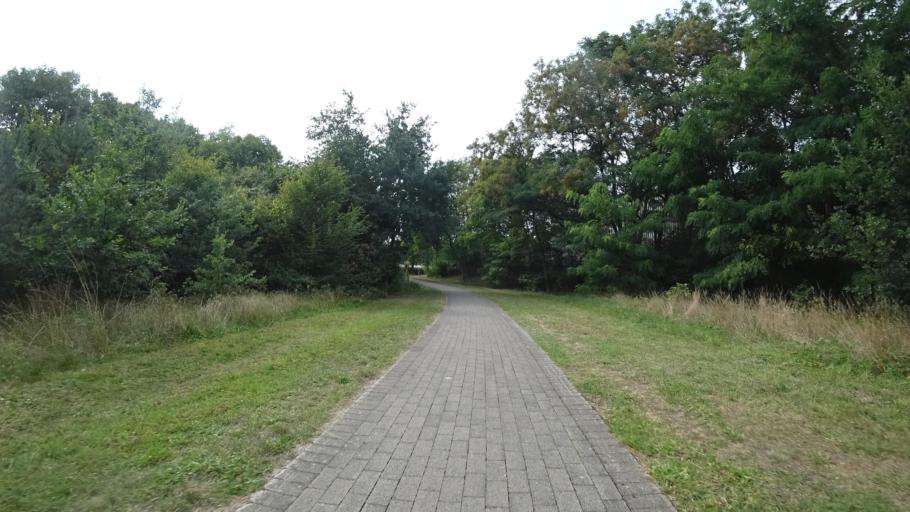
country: DE
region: North Rhine-Westphalia
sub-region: Regierungsbezirk Detmold
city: Guetersloh
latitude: 51.9172
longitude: 8.4084
